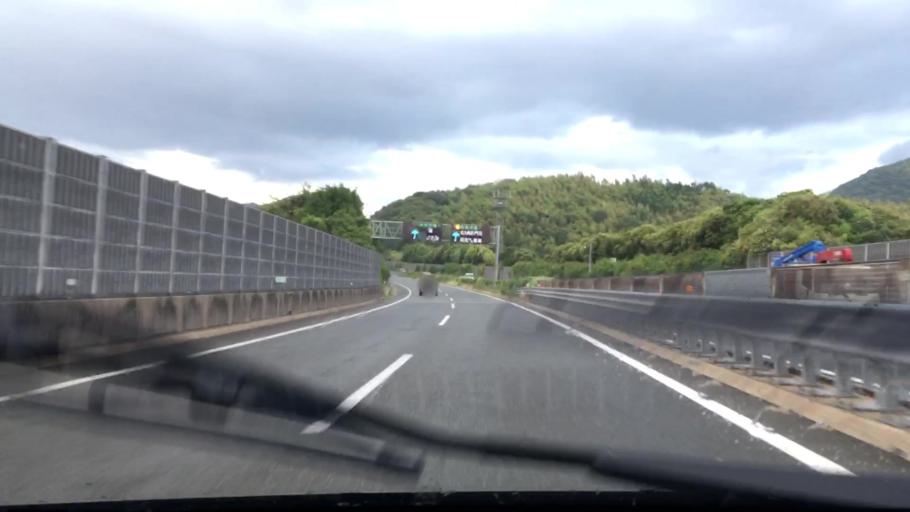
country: JP
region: Fukuoka
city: Kitakyushu
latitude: 33.8061
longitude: 130.8763
